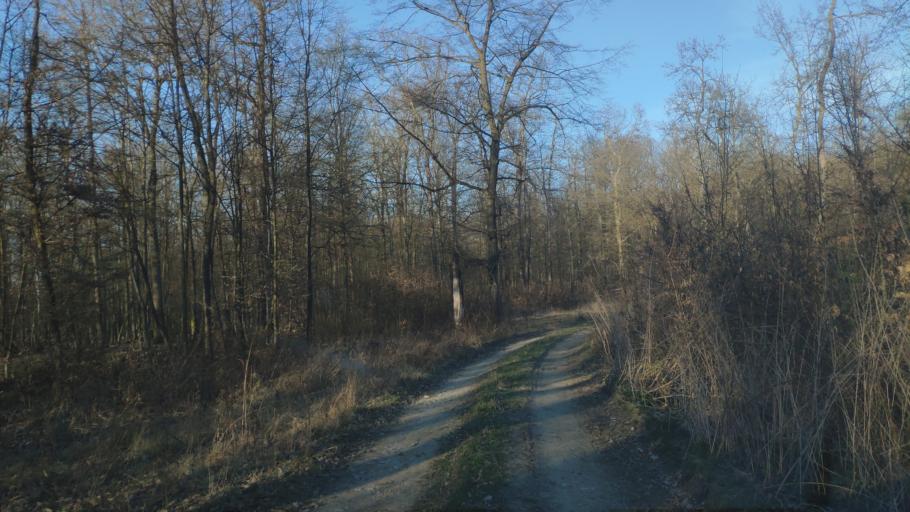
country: HU
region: Borsod-Abauj-Zemplen
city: Putnok
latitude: 48.5058
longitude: 20.3093
